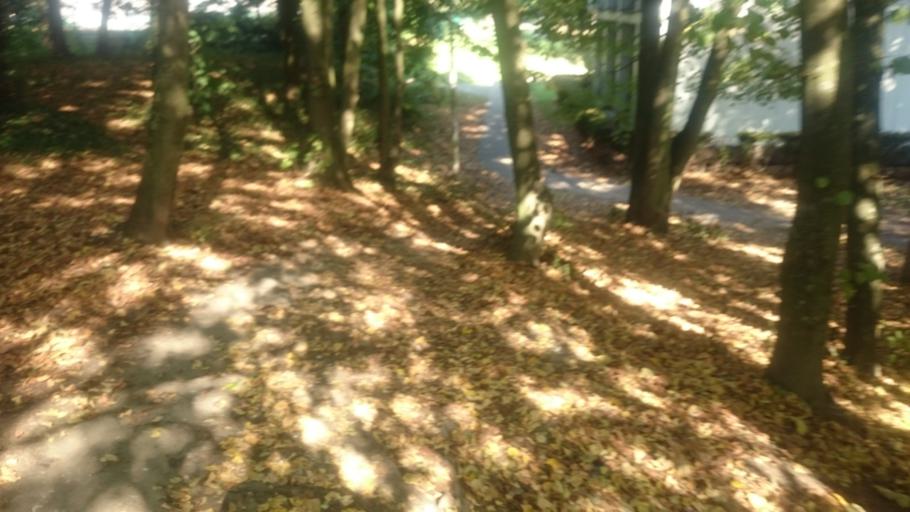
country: BE
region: Brussels Capital
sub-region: Bruxelles-Capitale
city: Brussels
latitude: 50.8222
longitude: 4.3953
